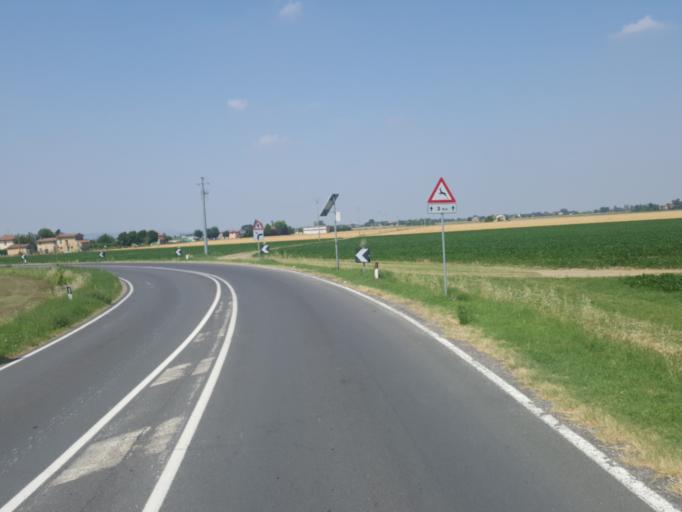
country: IT
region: Emilia-Romagna
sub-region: Provincia di Bologna
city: Castel Guelfo di Bologna
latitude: 44.4367
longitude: 11.6560
